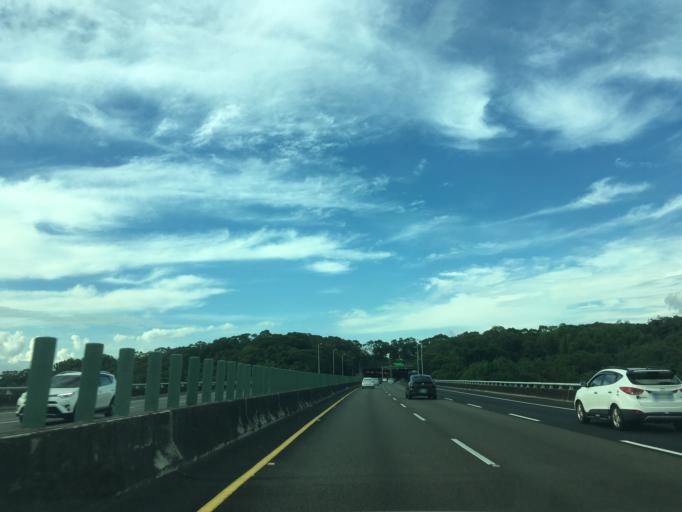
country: TW
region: Taiwan
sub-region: Chiayi
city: Jiayi Shi
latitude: 23.5731
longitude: 120.5063
